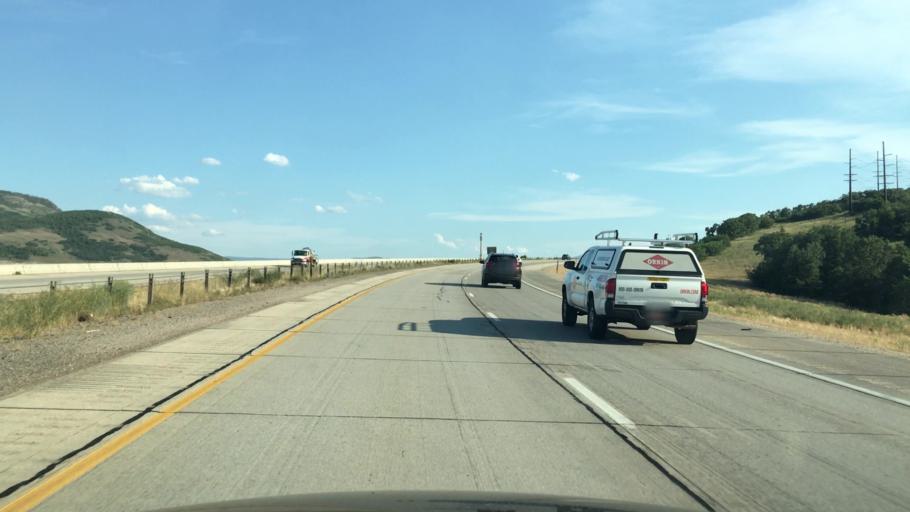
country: US
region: Utah
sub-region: Summit County
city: Park City
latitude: 40.6071
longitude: -111.4290
